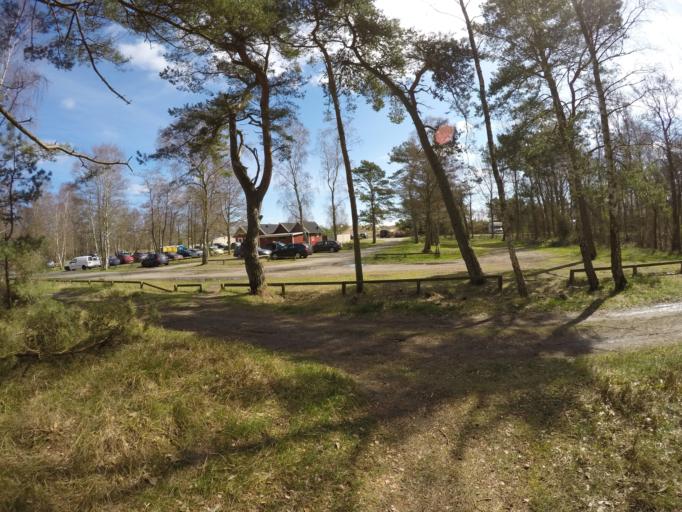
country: SE
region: Skane
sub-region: Simrishamns Kommun
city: Simrishamn
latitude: 55.3862
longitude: 14.1946
